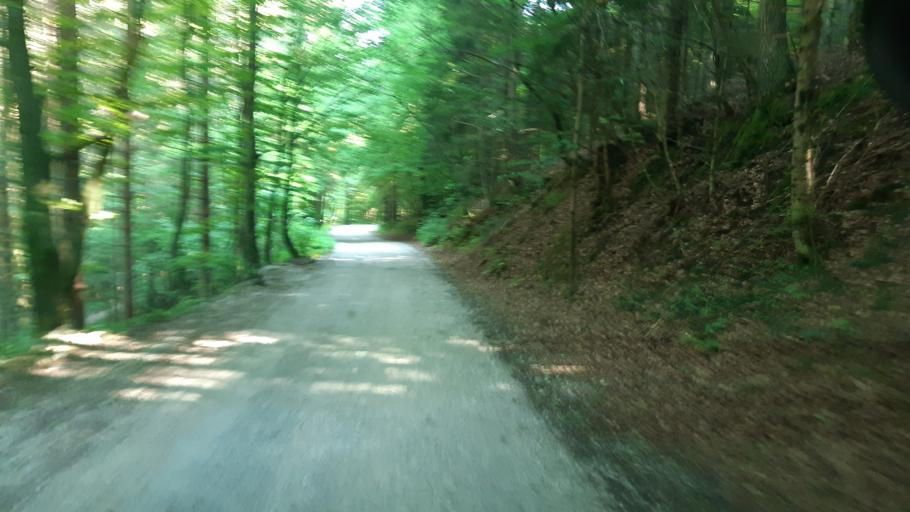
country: SI
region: Trzic
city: Bistrica pri Trzicu
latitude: 46.3692
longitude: 14.2772
